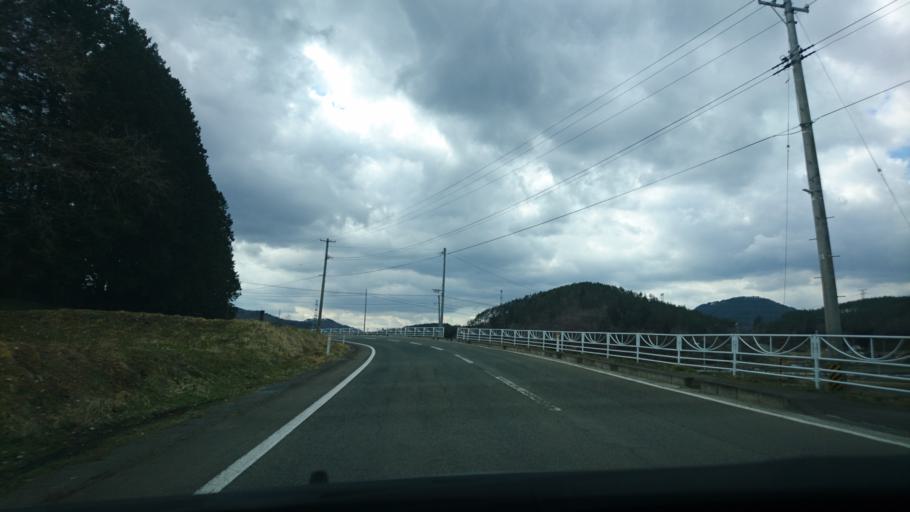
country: JP
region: Iwate
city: Tono
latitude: 39.3530
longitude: 141.3453
